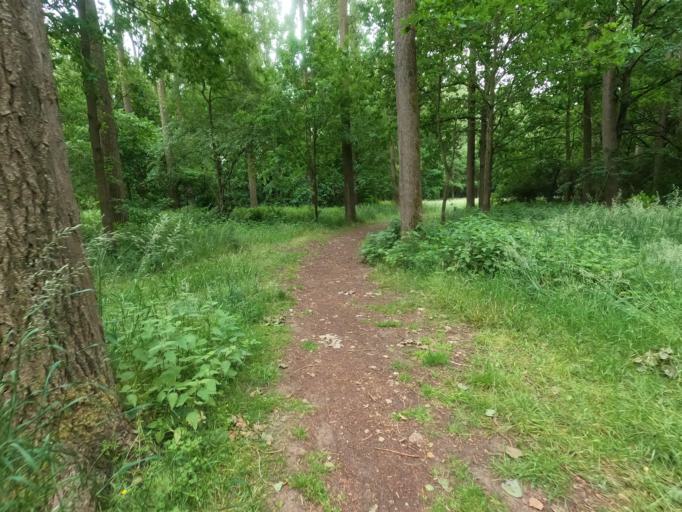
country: BE
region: Flanders
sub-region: Provincie Vlaams-Brabant
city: Tremelo
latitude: 50.9857
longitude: 4.7167
